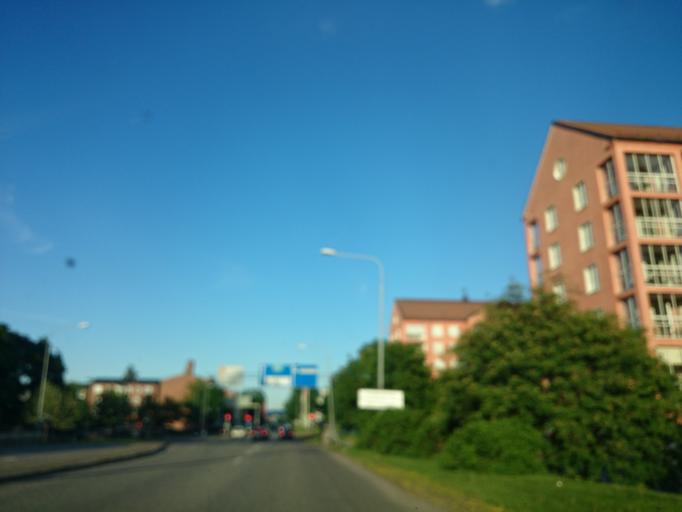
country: SE
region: Vaesternorrland
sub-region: Sundsvalls Kommun
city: Sundsvall
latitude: 62.3869
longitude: 17.2970
